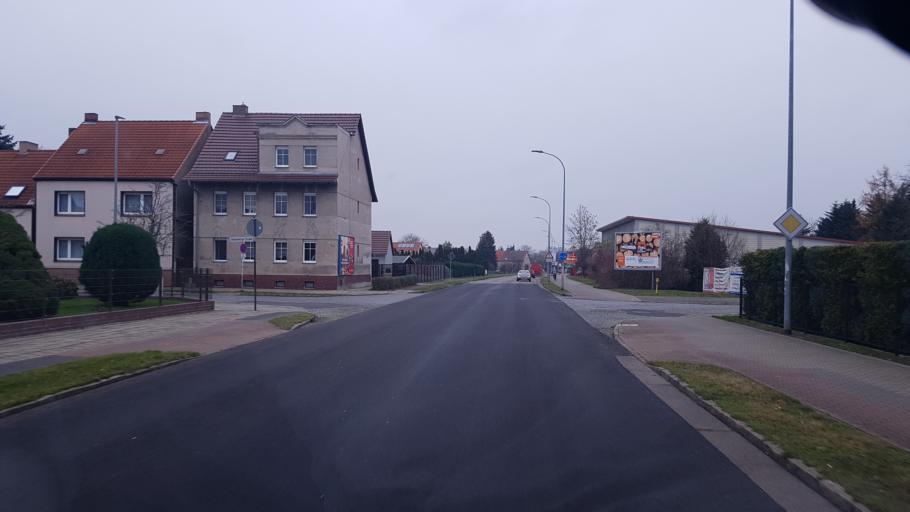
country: DE
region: Brandenburg
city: Guben
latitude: 51.9497
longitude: 14.7028
